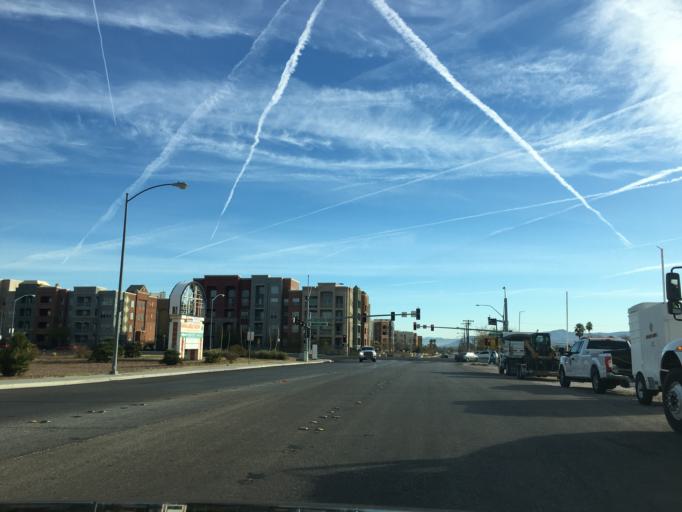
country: US
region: Nevada
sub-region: Clark County
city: Enterprise
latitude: 36.0210
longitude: -115.1736
